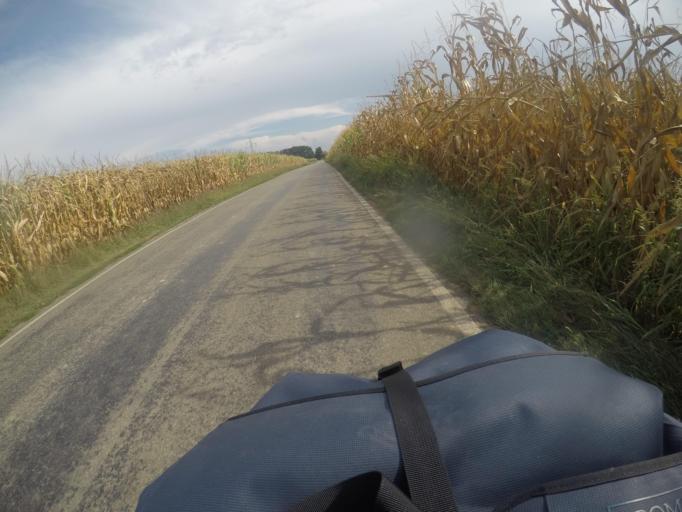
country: DE
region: Baden-Wuerttemberg
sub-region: Freiburg Region
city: Efringen-Kirchen
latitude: 47.6361
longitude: 7.5715
